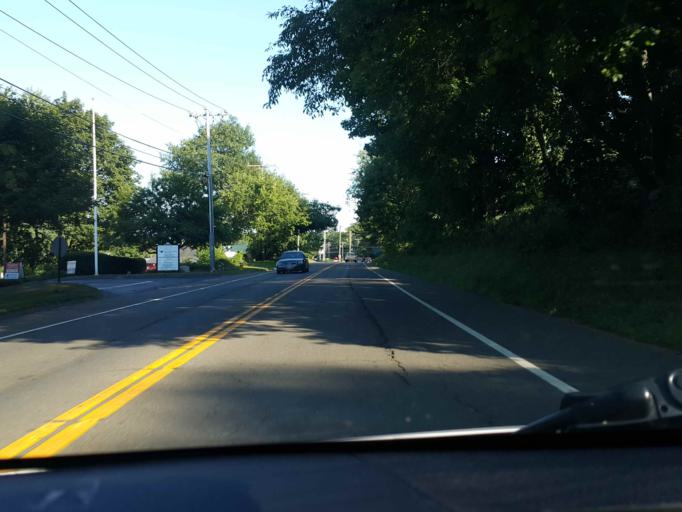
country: US
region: Connecticut
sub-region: New Haven County
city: Guilford
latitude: 41.2917
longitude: -72.6973
